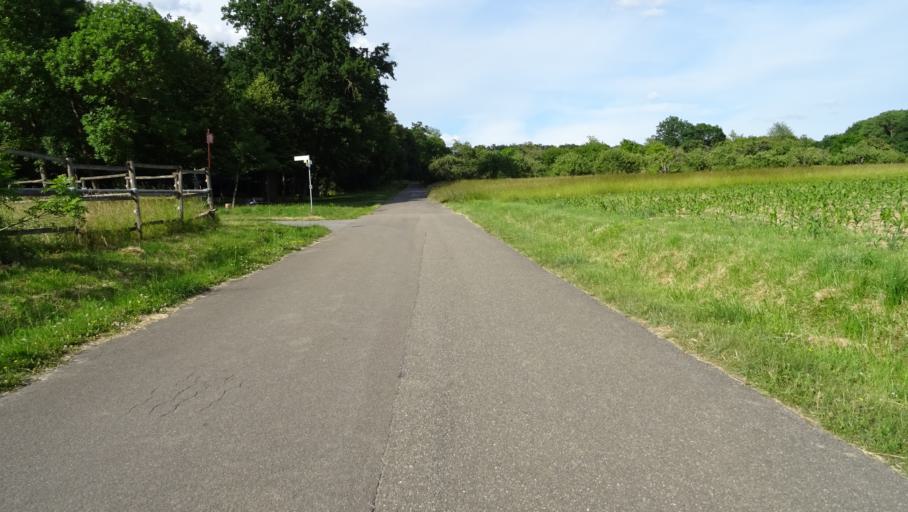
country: DE
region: Baden-Wuerttemberg
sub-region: Regierungsbezirk Stuttgart
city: Offenau
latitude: 49.2523
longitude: 9.1691
